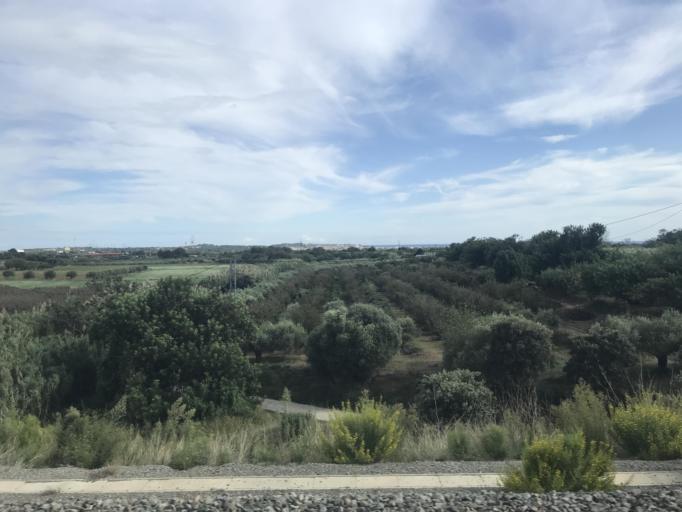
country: ES
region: Catalonia
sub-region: Provincia de Tarragona
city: Vila-seca
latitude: 41.1072
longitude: 1.1048
